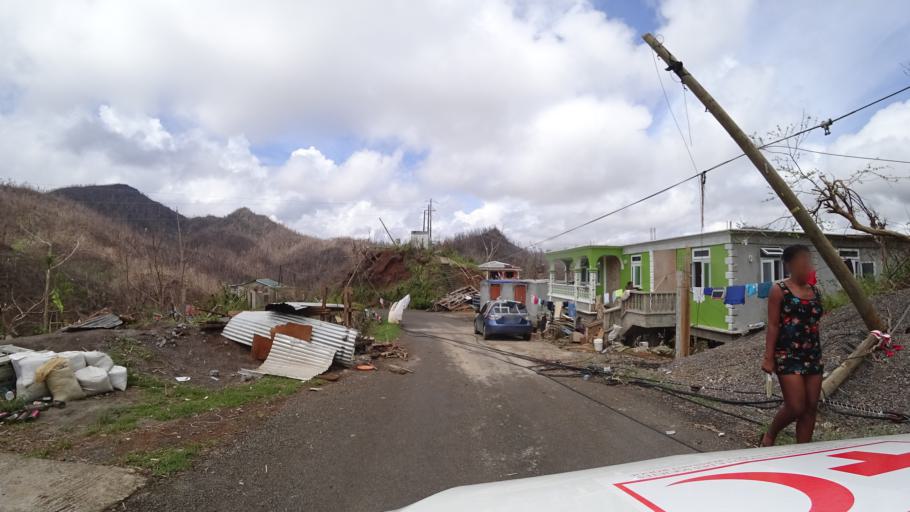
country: DM
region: Saint David
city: Rosalie
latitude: 15.3940
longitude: -61.2602
